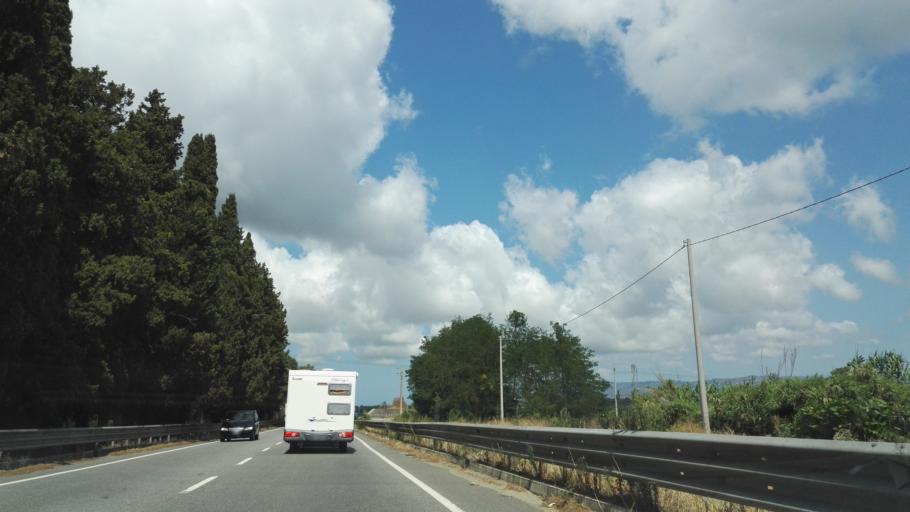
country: IT
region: Calabria
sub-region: Provincia di Reggio Calabria
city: Rosarno
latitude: 38.4604
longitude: 16.0179
